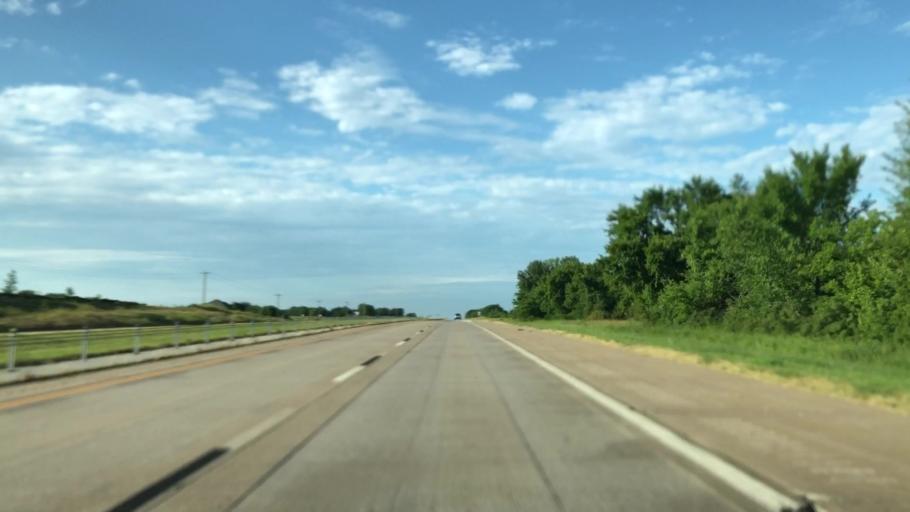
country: US
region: Oklahoma
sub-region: Osage County
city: Skiatook
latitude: 36.4363
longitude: -95.9207
